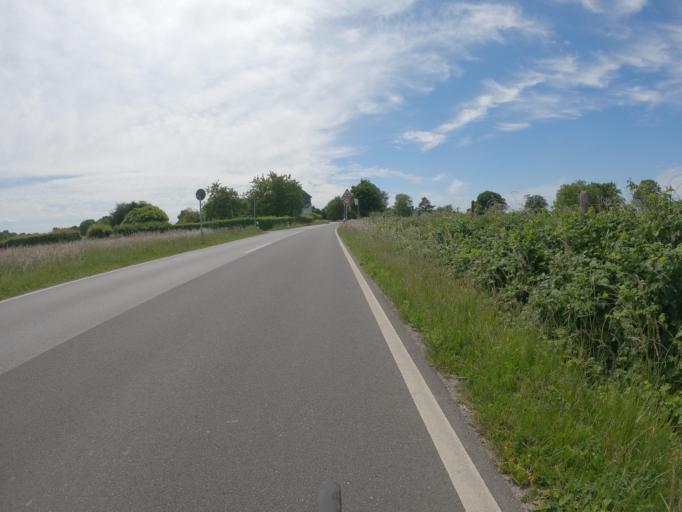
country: BE
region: Wallonia
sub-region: Province de Liege
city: Raeren
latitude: 50.7340
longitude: 6.1457
